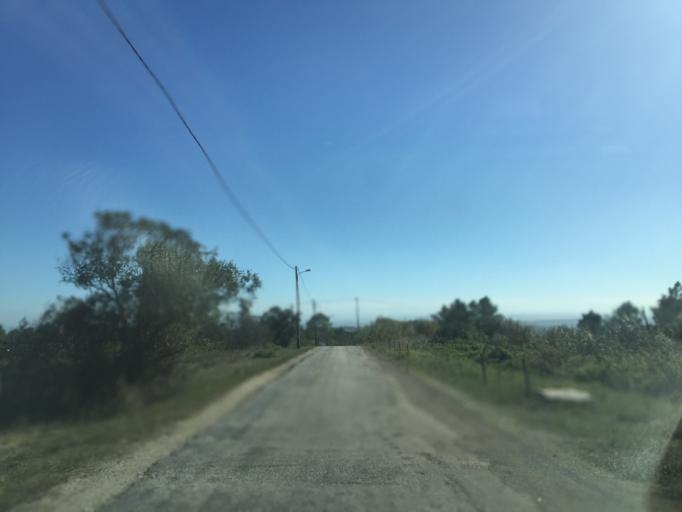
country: PT
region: Coimbra
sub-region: Figueira da Foz
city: Tavarede
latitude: 40.1913
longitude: -8.8380
